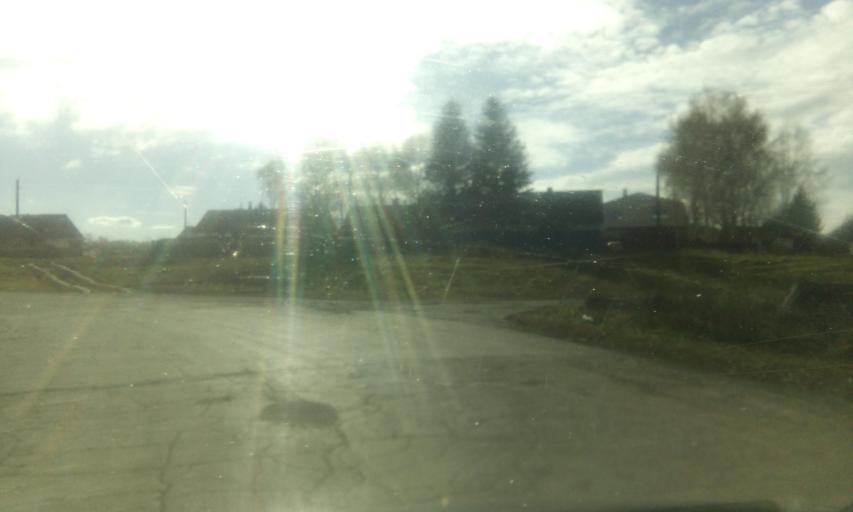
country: RU
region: Tula
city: Dubovka
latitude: 53.9472
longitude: 38.0276
